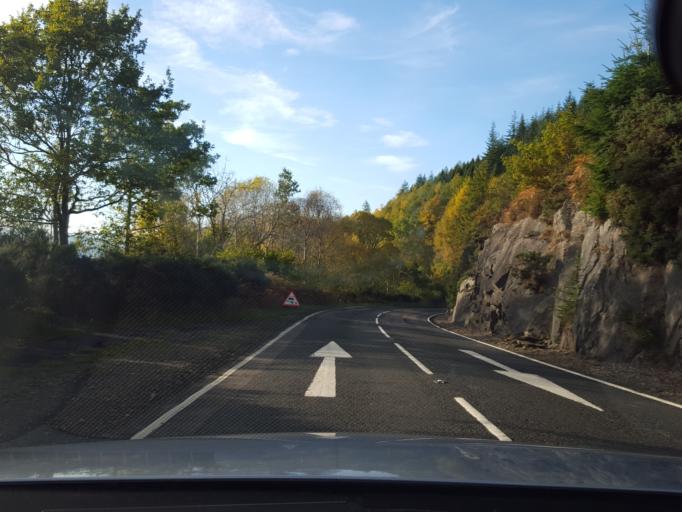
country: GB
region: Scotland
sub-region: Highland
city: Beauly
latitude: 57.3439
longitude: -4.4216
